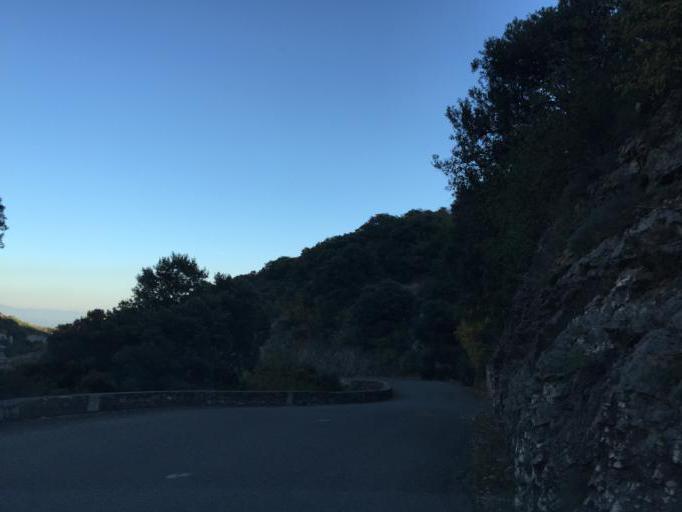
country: FR
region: Rhone-Alpes
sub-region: Departement de l'Ardeche
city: Bourg-Saint-Andeol
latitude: 44.4448
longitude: 4.6122
